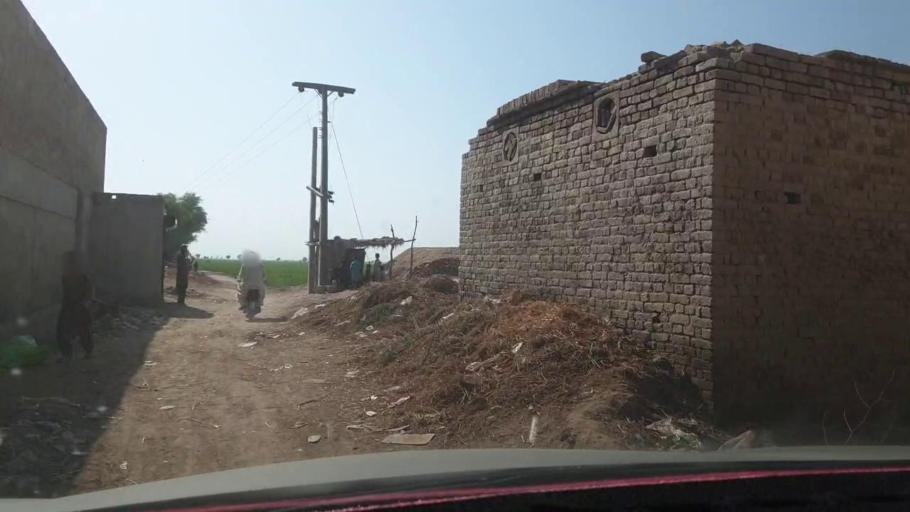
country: PK
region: Sindh
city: Nasirabad
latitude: 27.3853
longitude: 67.8711
